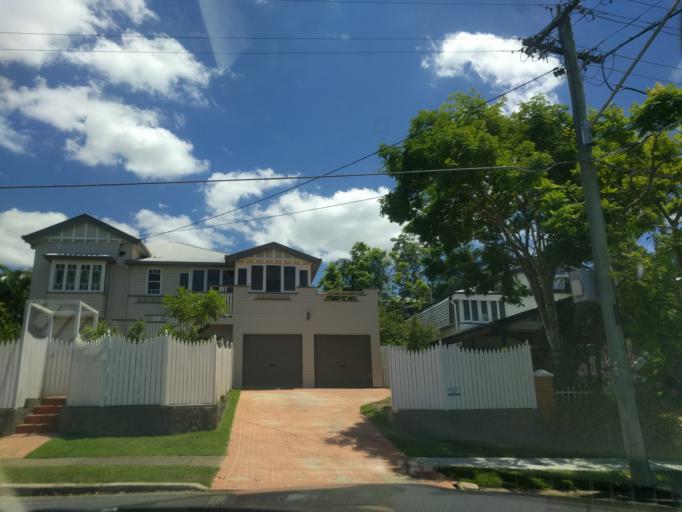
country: AU
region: Queensland
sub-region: Brisbane
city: Gordon Park
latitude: -27.4189
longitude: 153.0246
